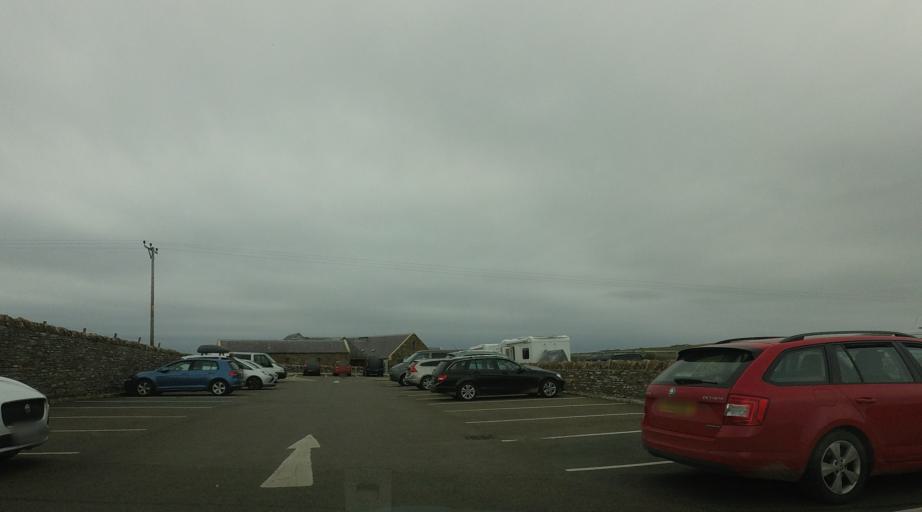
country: GB
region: Scotland
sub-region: Orkney Islands
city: Stromness
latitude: 59.0484
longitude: -3.3346
